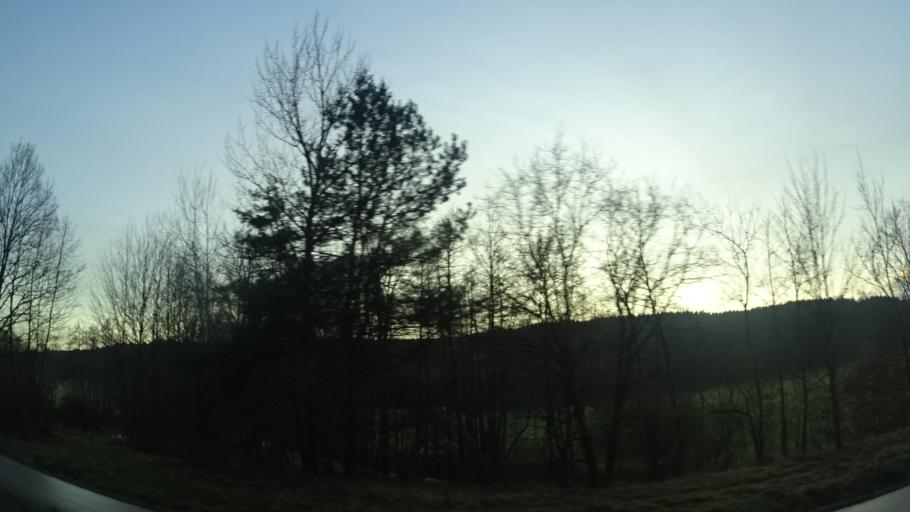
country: DE
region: Bavaria
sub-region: Regierungsbezirk Unterfranken
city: Oberelsbach
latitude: 50.3773
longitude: 10.1143
